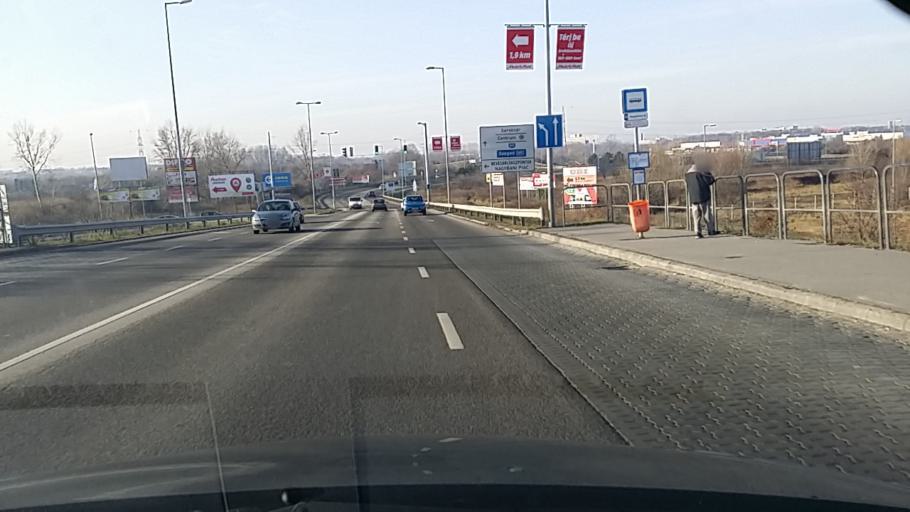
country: HU
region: Budapest
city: Budapest XVIII. keruelet
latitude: 47.4253
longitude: 19.1572
